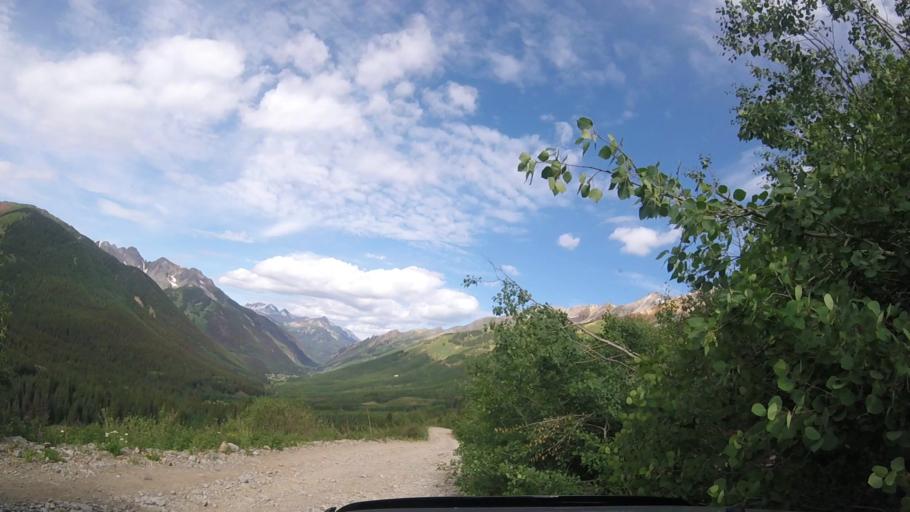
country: US
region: Colorado
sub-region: San Miguel County
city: Telluride
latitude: 37.8580
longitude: -107.7912
